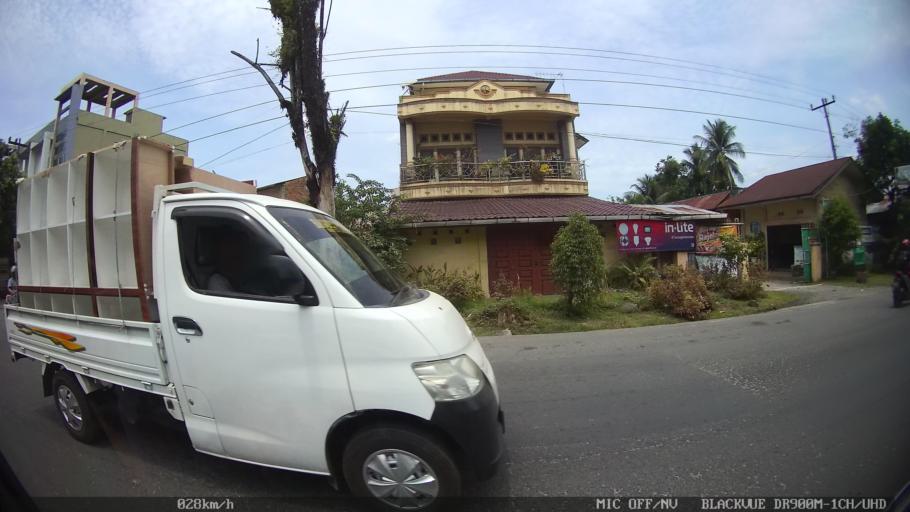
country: ID
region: North Sumatra
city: Sunggal
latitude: 3.5246
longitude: 98.6198
